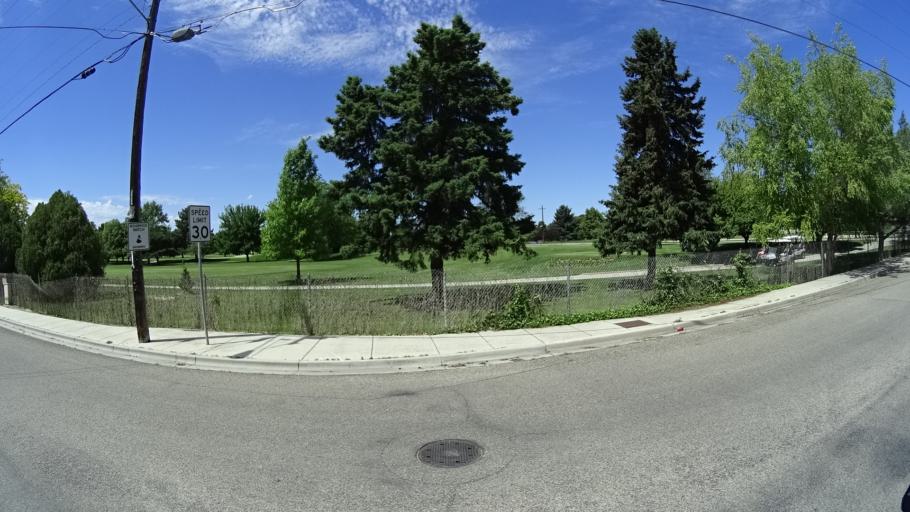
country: US
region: Idaho
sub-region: Ada County
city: Garden City
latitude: 43.5817
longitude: -116.2336
